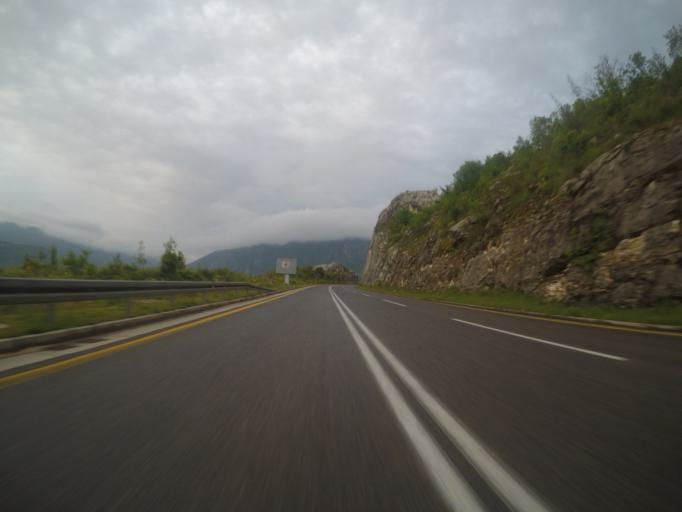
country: ME
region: Bar
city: Sutomore
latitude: 42.2217
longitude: 19.0514
